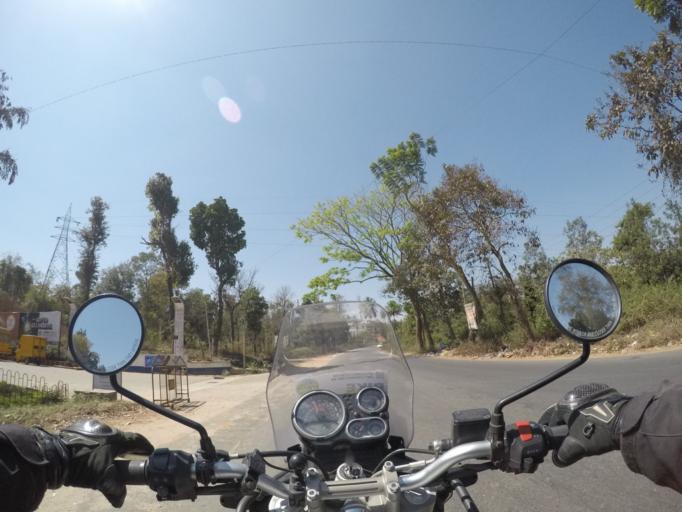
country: IN
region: Karnataka
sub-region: Hassan
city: Sakleshpur
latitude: 12.9489
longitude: 75.8089
